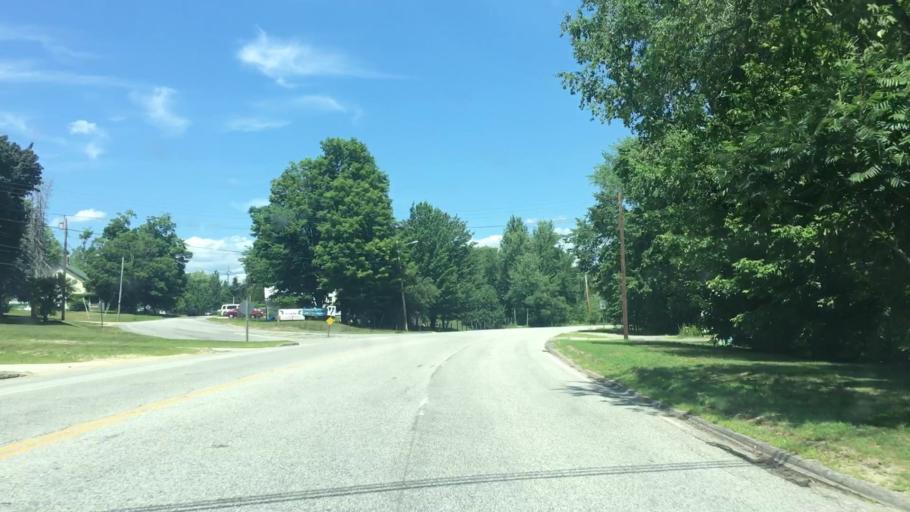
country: US
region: Maine
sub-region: Franklin County
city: Chisholm
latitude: 44.4406
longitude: -70.2166
